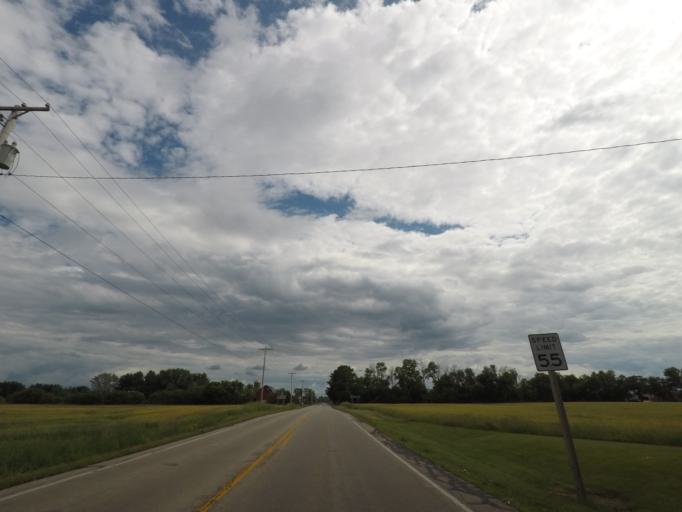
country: US
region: Wisconsin
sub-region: Dane County
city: Belleville
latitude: 42.8556
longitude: -89.5235
